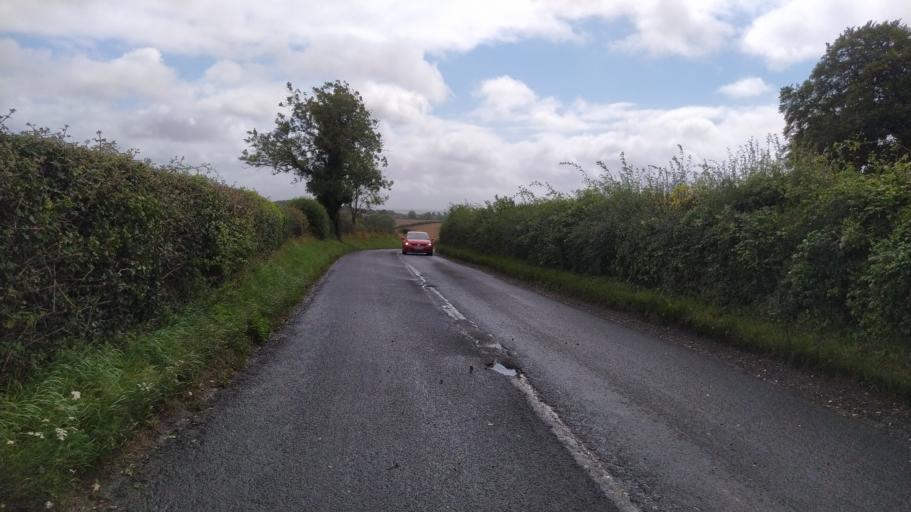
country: GB
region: England
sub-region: Wiltshire
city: Ansty
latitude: 50.9604
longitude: -2.1029
